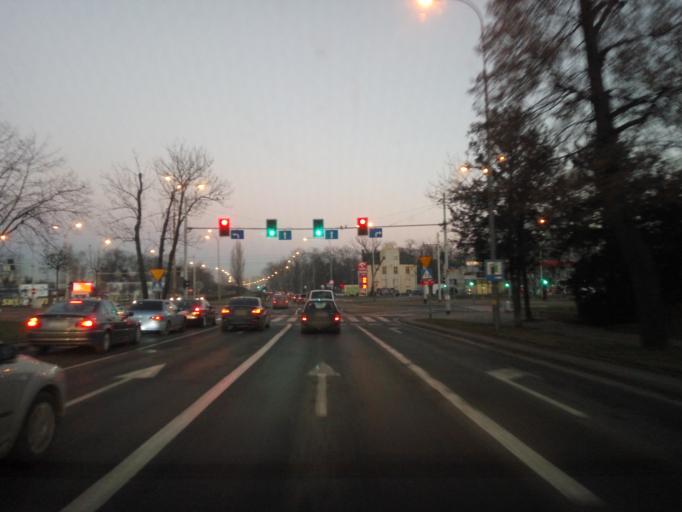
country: PL
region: Lower Silesian Voivodeship
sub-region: Powiat wroclawski
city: Wroclaw
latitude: 51.0840
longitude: 17.0240
